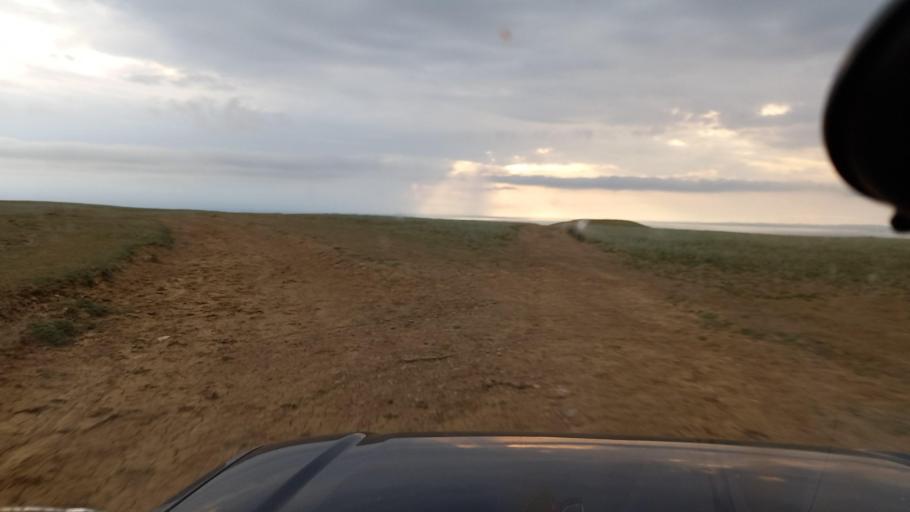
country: RU
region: Krasnodarskiy
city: Taman'
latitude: 45.2070
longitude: 36.7865
